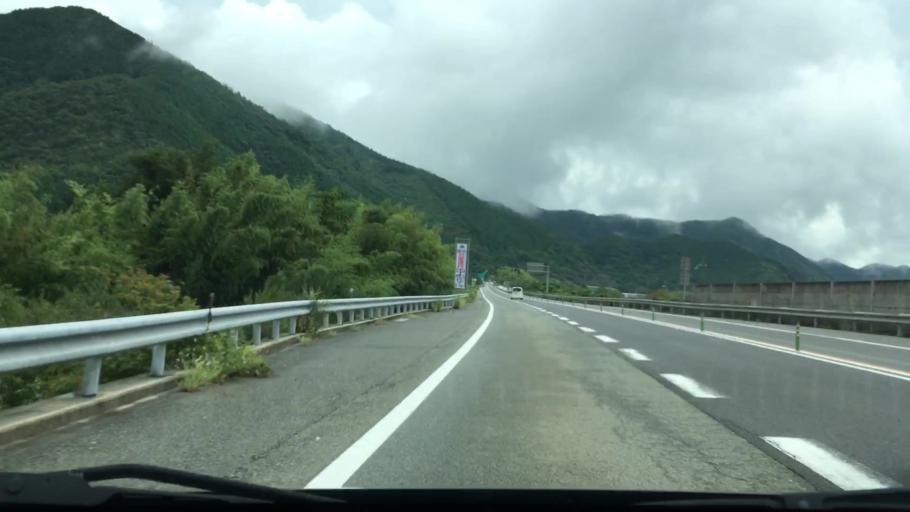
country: JP
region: Hyogo
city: Nishiwaki
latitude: 35.0485
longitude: 134.7646
